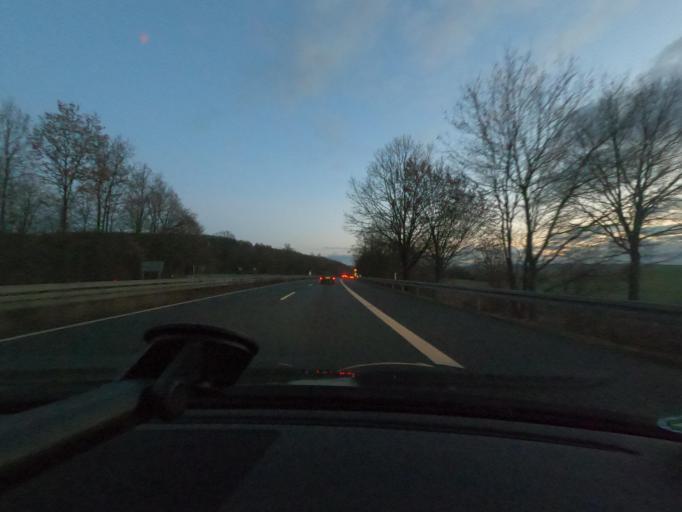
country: DE
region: Lower Saxony
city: Herzberg am Harz
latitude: 51.6397
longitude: 10.3612
